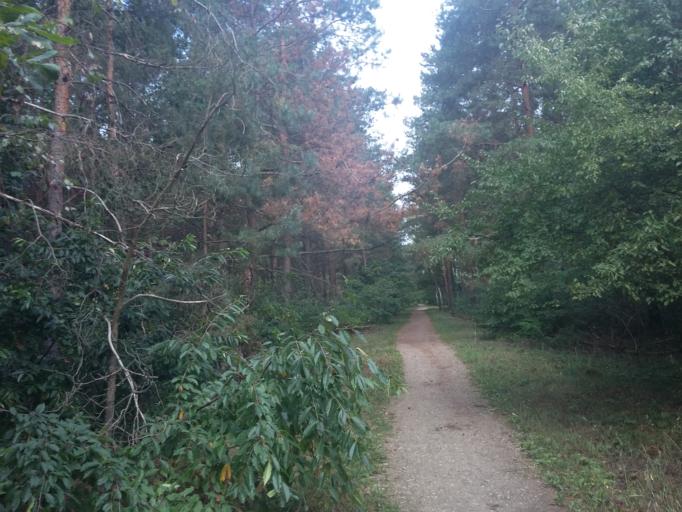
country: PL
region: Lodz Voivodeship
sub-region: Powiat pabianicki
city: Ksawerow
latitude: 51.7240
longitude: 19.3875
